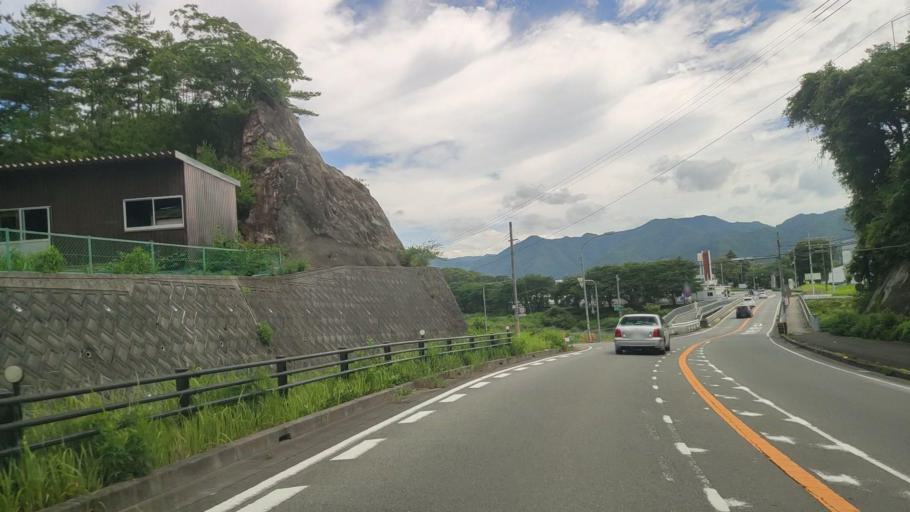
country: JP
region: Hyogo
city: Nishiwaki
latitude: 35.0554
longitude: 134.9170
